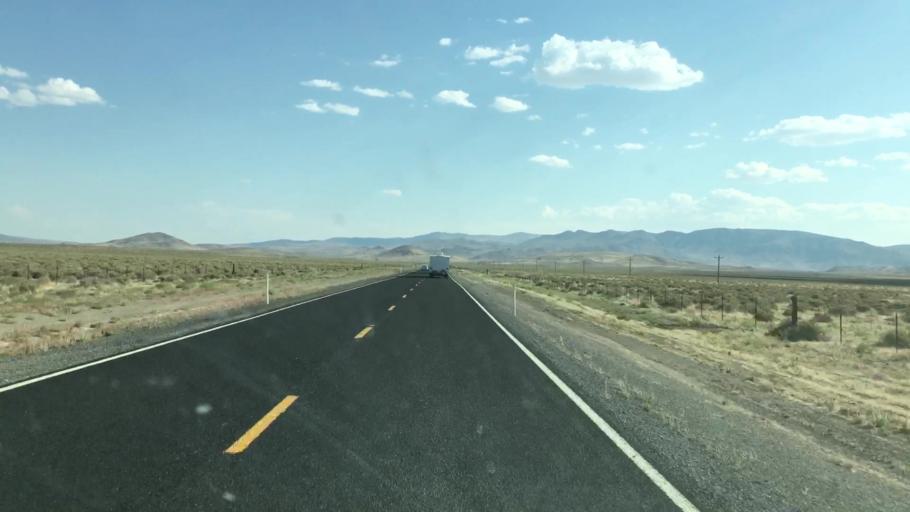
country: US
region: Nevada
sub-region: Lyon County
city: Fernley
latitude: 39.6746
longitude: -119.3330
